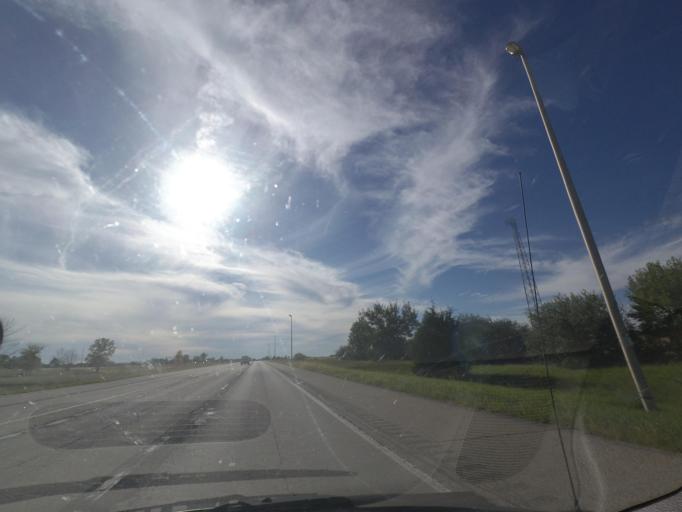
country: US
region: Illinois
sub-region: Macon County
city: Harristown
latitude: 39.8375
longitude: -89.0538
